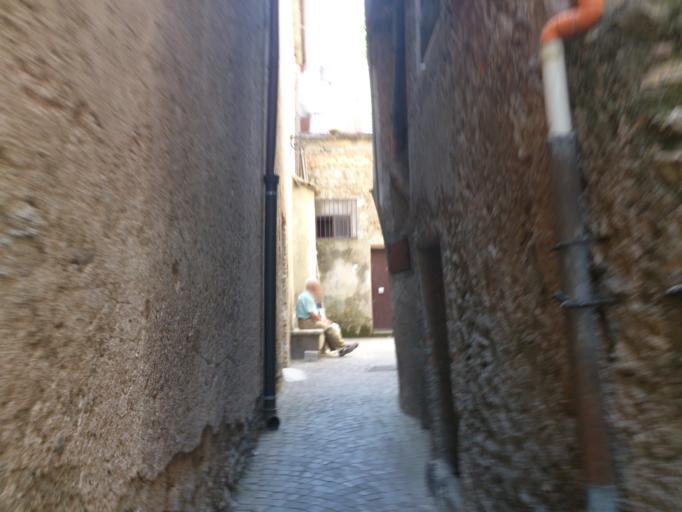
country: IT
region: Calabria
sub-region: Provincia di Reggio Calabria
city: Pazzano
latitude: 38.4760
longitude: 16.4517
